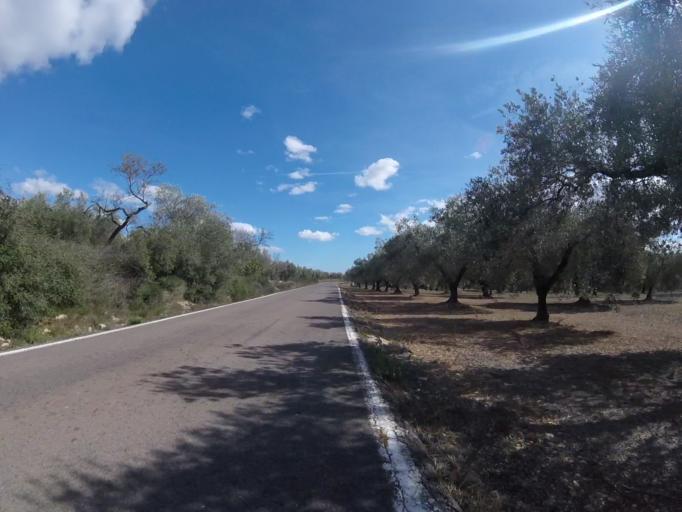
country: ES
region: Valencia
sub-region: Provincia de Castello
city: Albocasser
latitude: 40.4024
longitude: 0.0829
